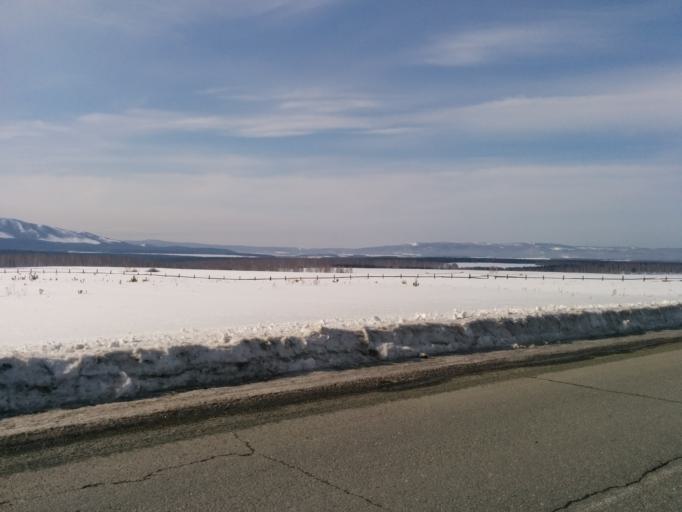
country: RU
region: Bashkortostan
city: Lomovka
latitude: 53.8296
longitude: 58.2810
